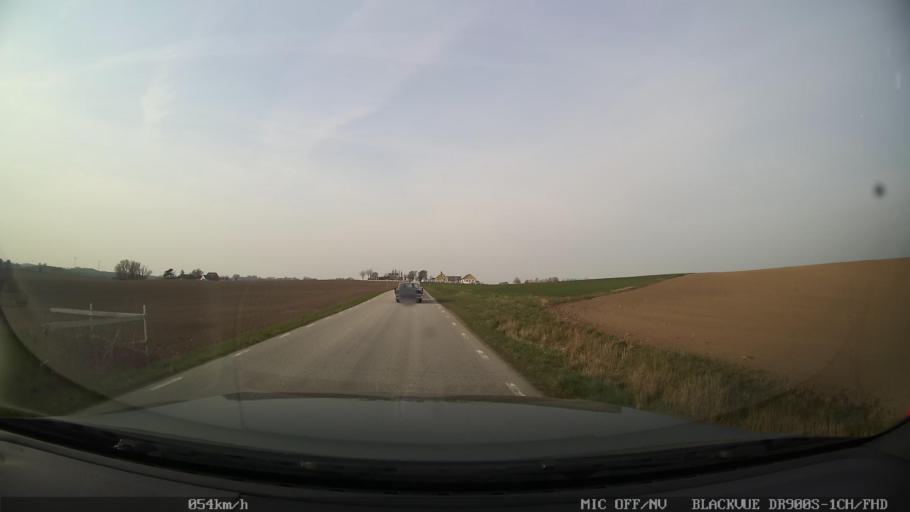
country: SE
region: Skane
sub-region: Ystads Kommun
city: Ystad
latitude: 55.4550
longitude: 13.8298
